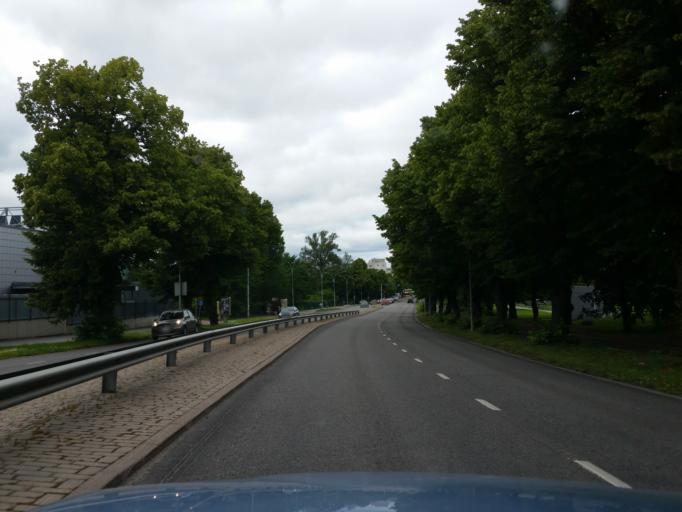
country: FI
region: Varsinais-Suomi
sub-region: Turku
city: Turku
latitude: 60.4419
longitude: 22.2885
